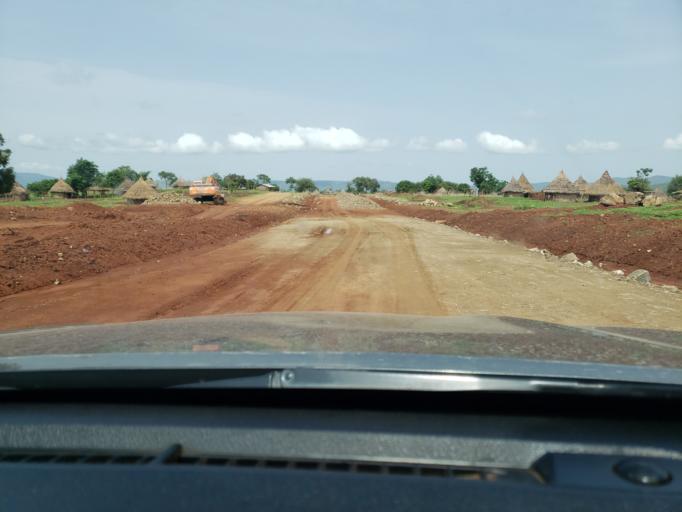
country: ET
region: Oromiya
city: Mendi
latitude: 10.1195
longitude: 35.1461
